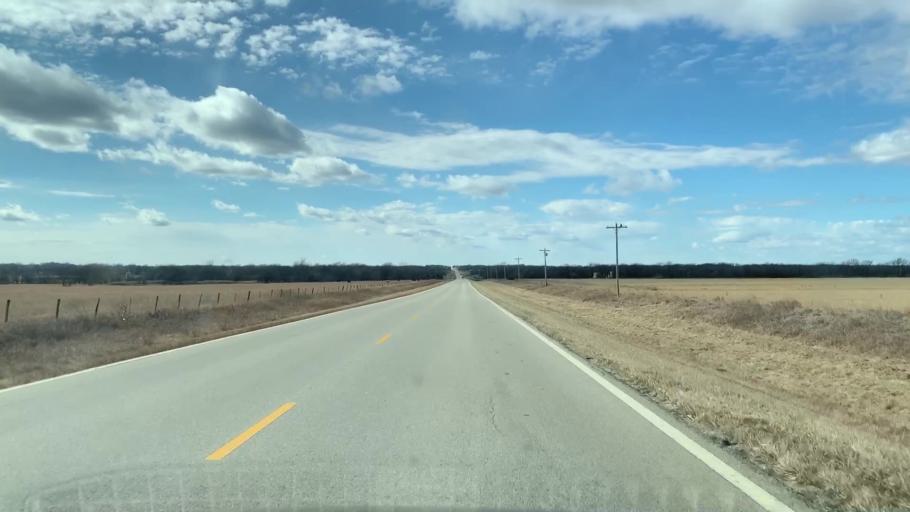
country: US
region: Kansas
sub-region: Neosho County
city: Erie
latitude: 37.5292
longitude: -95.3910
